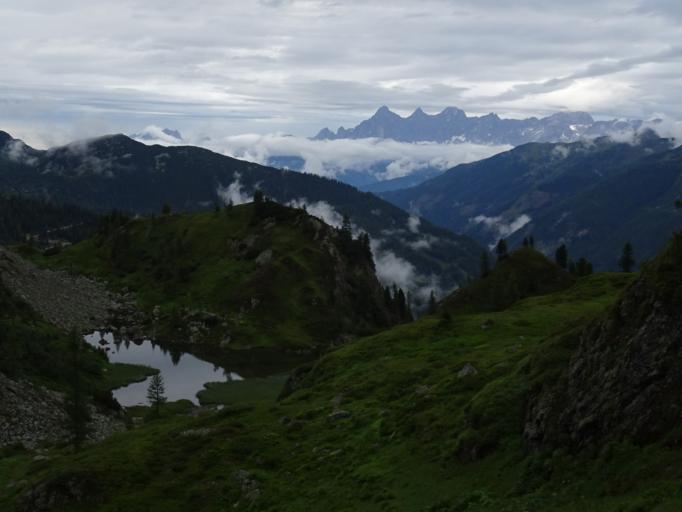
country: AT
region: Salzburg
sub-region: Politischer Bezirk Sankt Johann im Pongau
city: Untertauern
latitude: 47.2740
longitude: 13.5676
